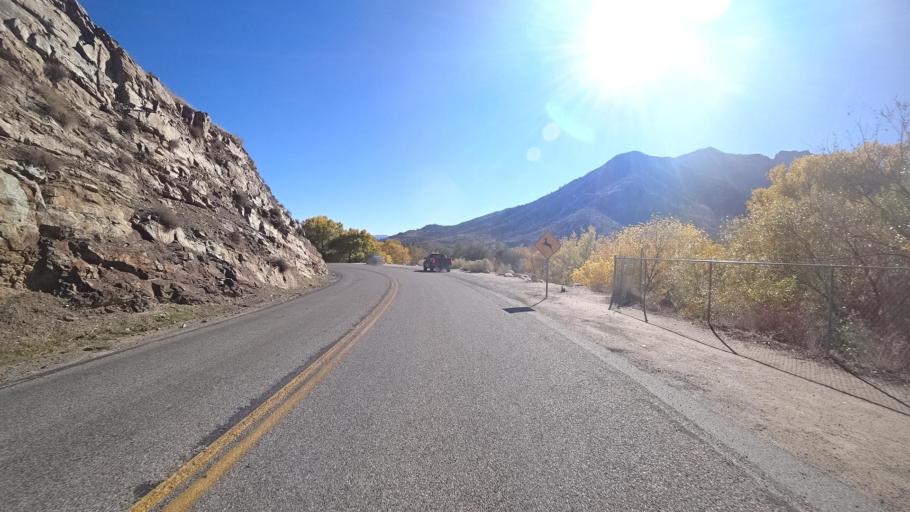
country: US
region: California
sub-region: Kern County
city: Kernville
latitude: 35.7851
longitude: -118.4465
